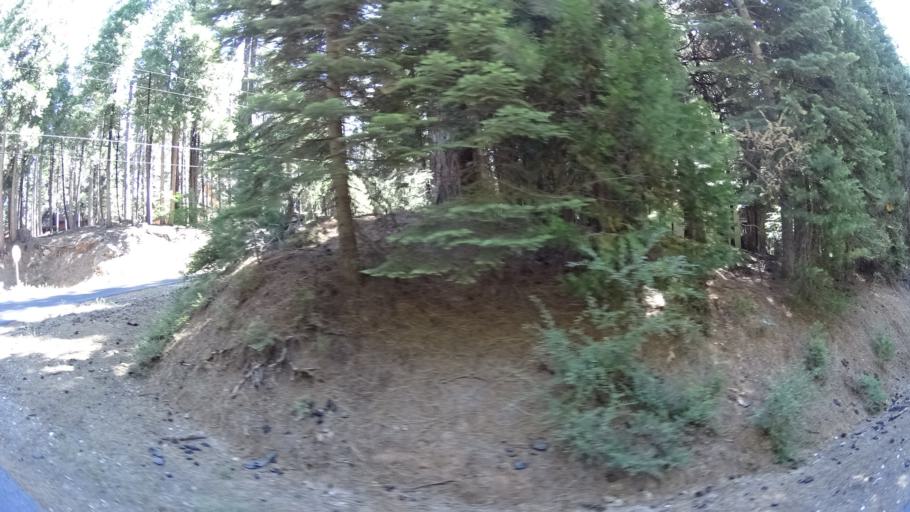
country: US
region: California
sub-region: Calaveras County
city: Arnold
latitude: 38.2895
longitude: -120.2783
